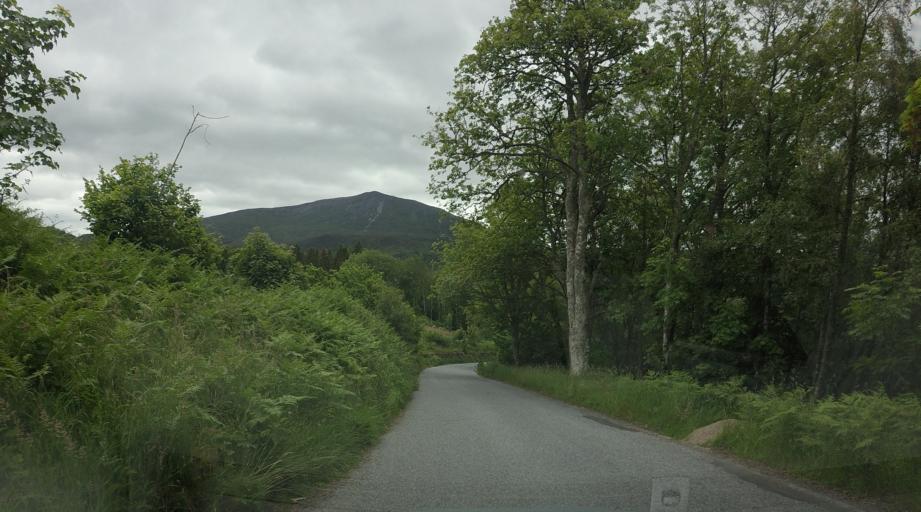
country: GB
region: Scotland
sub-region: Perth and Kinross
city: Aberfeldy
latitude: 56.7071
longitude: -4.1134
